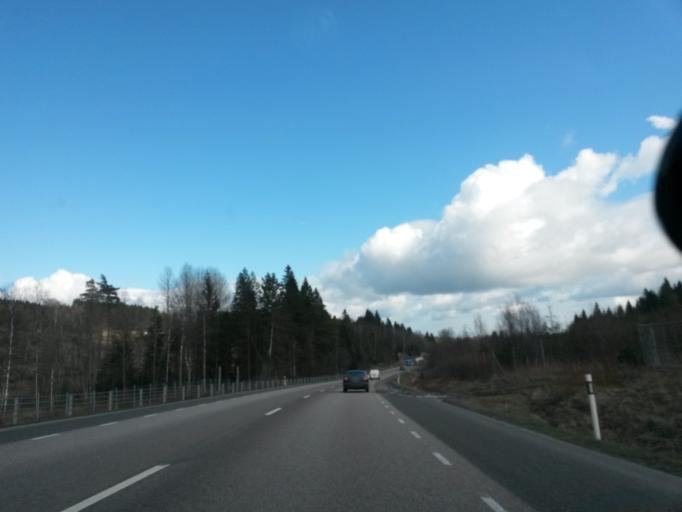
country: SE
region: Vaestra Goetaland
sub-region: Skovde Kommun
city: Skoevde
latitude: 58.3937
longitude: 13.7710
